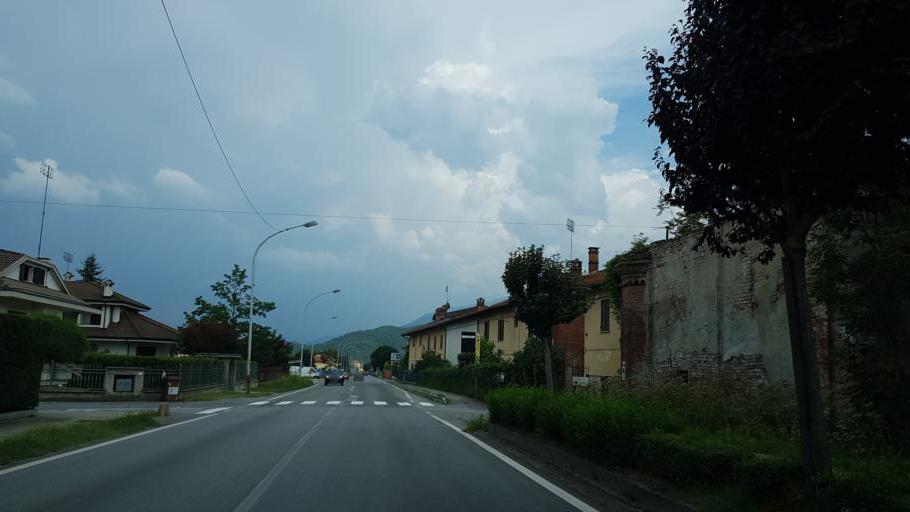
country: IT
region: Piedmont
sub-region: Provincia di Cuneo
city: Roccavione
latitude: 44.3327
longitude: 7.4730
